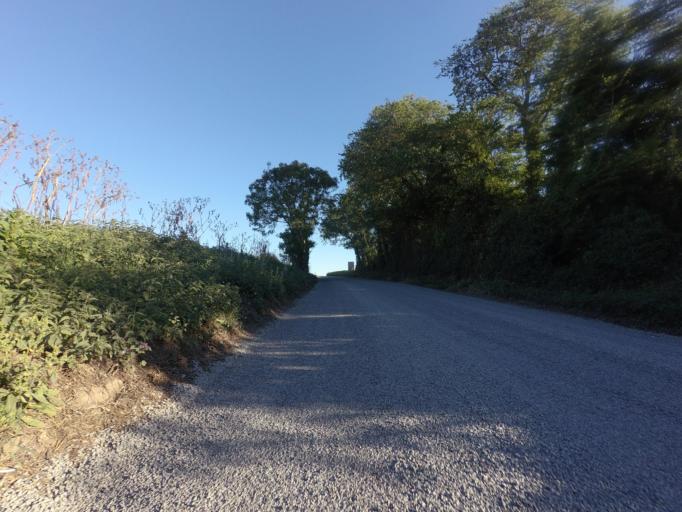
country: GB
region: England
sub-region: Kent
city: Herne Bay
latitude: 51.3414
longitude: 1.1898
